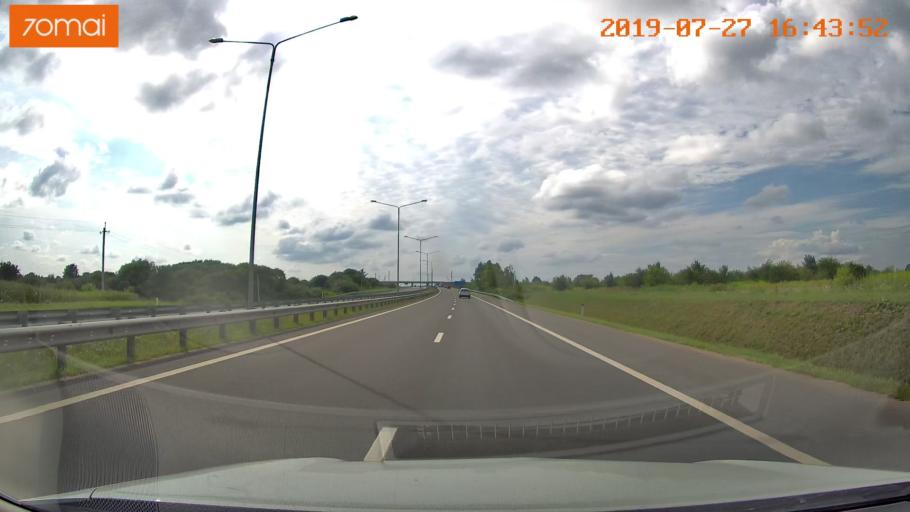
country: RU
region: Kaliningrad
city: Gvardeysk
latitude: 54.6724
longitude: 21.0917
